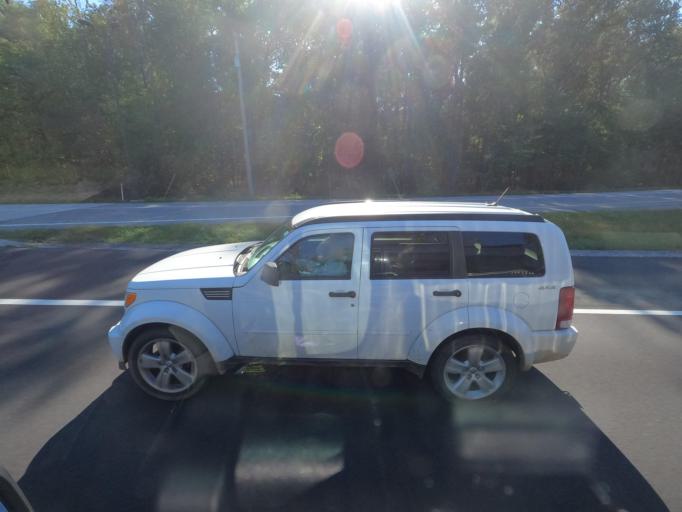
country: US
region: Tennessee
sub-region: Coffee County
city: Manchester
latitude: 35.4311
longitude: -86.0306
